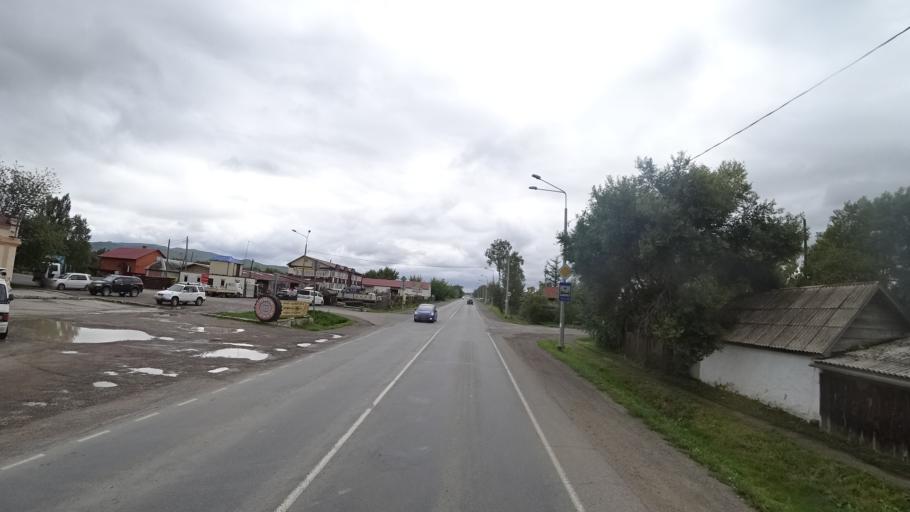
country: RU
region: Primorskiy
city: Chernigovka
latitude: 44.3361
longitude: 132.5829
